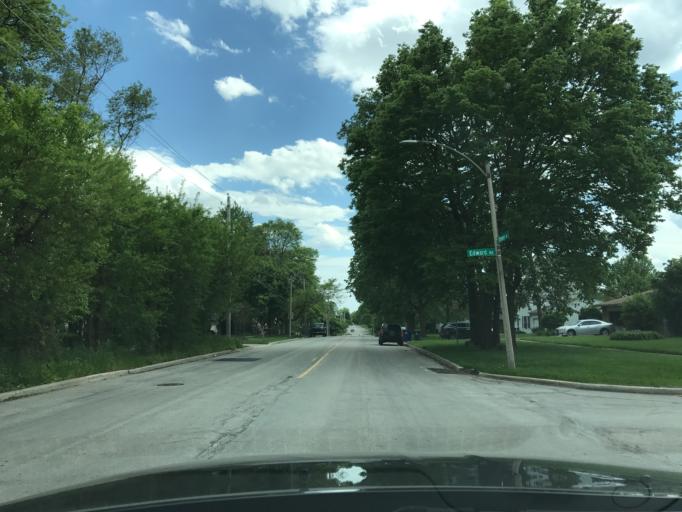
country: US
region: Illinois
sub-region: DuPage County
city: Naperville
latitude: 41.7681
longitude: -88.1205
